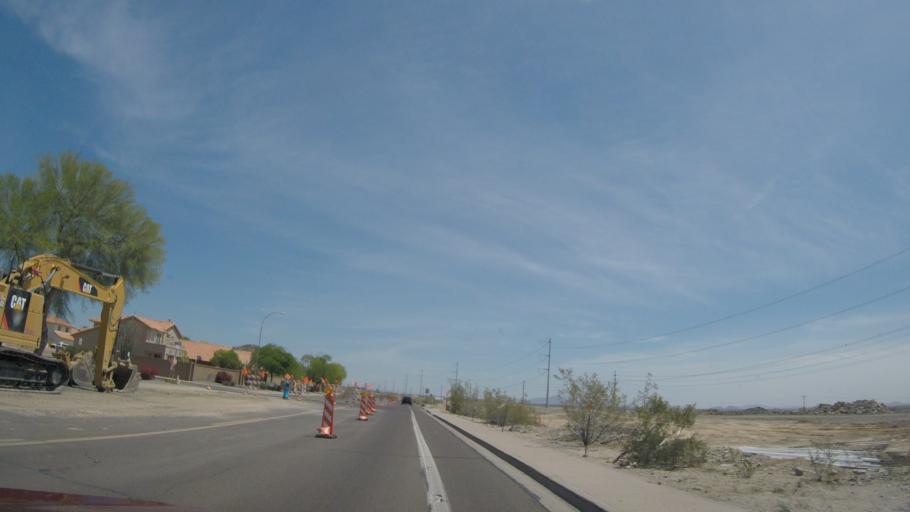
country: US
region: Arizona
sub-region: Maricopa County
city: Guadalupe
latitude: 33.2919
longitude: -112.0516
